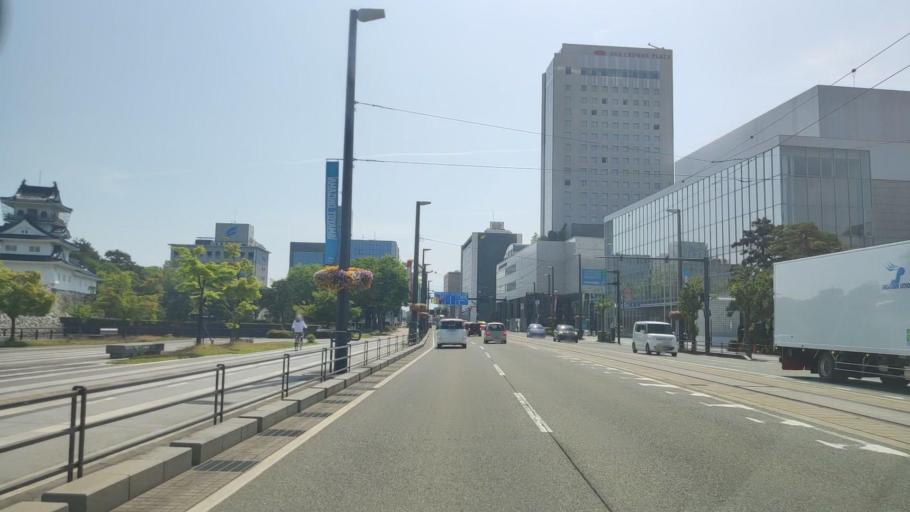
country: JP
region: Toyama
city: Toyama-shi
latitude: 36.6922
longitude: 137.2100
